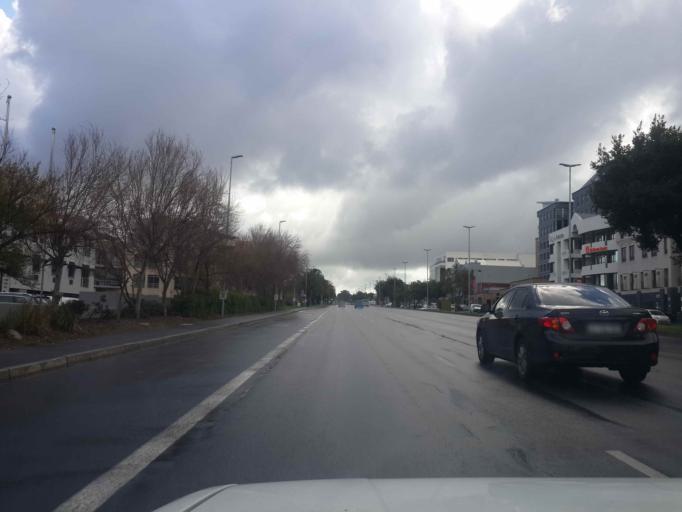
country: ZA
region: Western Cape
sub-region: City of Cape Town
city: Kraaifontein
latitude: -33.8822
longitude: 18.6350
